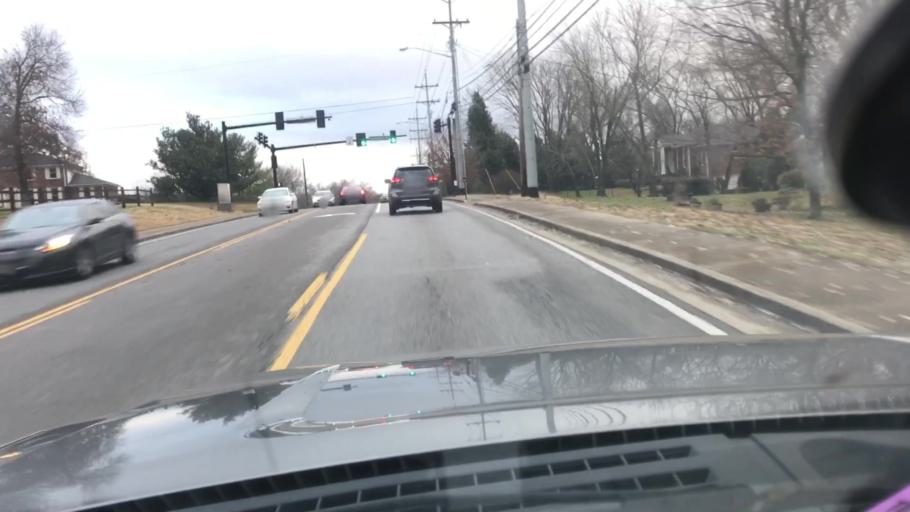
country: US
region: Tennessee
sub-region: Williamson County
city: Brentwood Estates
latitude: 35.9649
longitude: -86.7939
